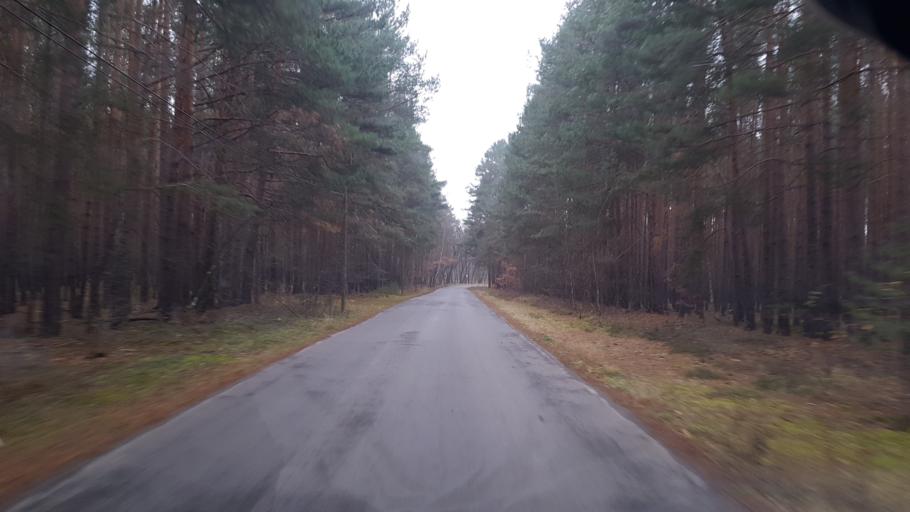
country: DE
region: Brandenburg
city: Calau
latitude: 51.7249
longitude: 14.0097
